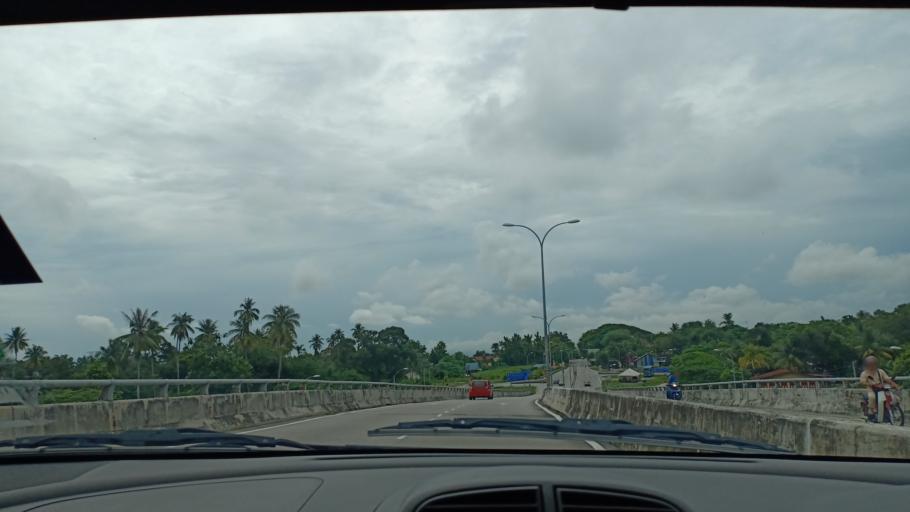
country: MY
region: Penang
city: Bukit Mertajam
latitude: 5.4062
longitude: 100.4728
